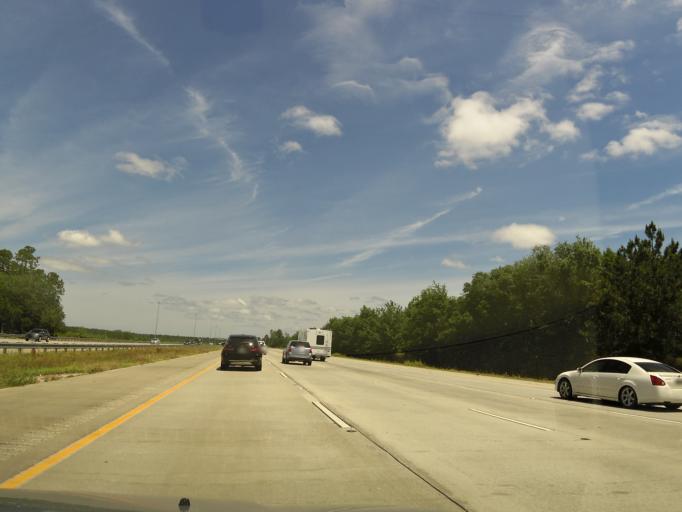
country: US
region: Georgia
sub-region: Glynn County
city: Country Club Estates
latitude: 31.2788
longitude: -81.4889
